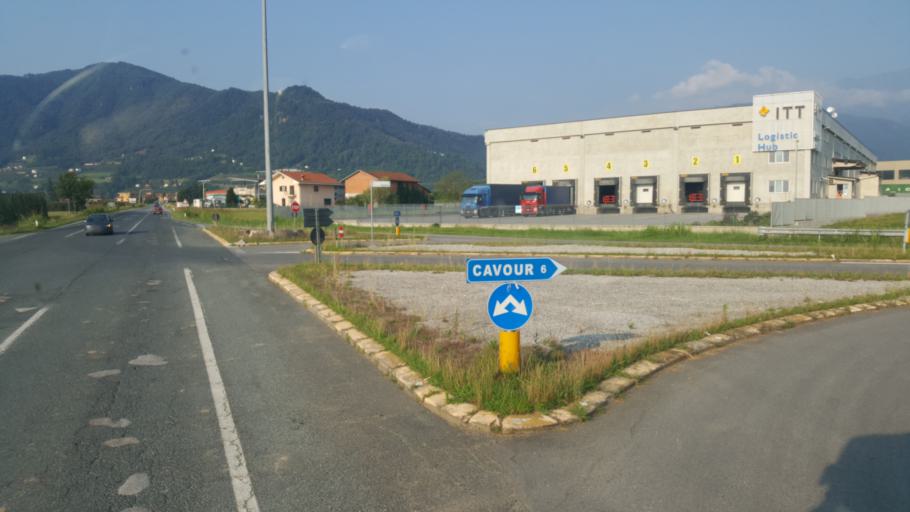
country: IT
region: Piedmont
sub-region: Provincia di Cuneo
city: Barge
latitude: 44.7364
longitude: 7.3610
